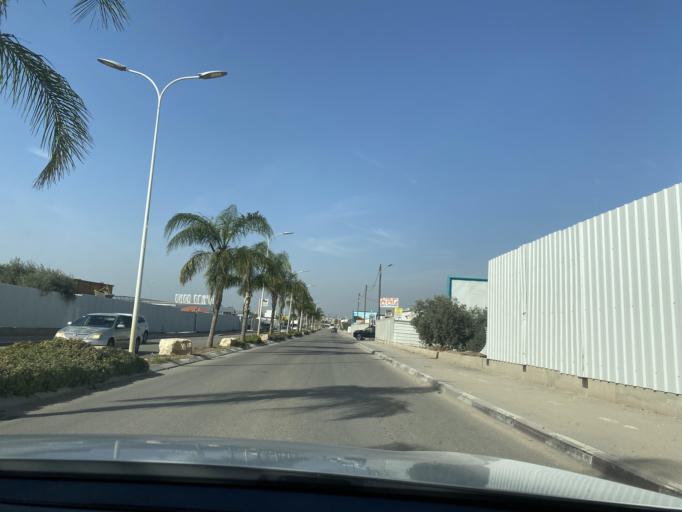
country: IL
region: Central District
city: Kafr Qasim
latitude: 32.1332
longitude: 34.9641
